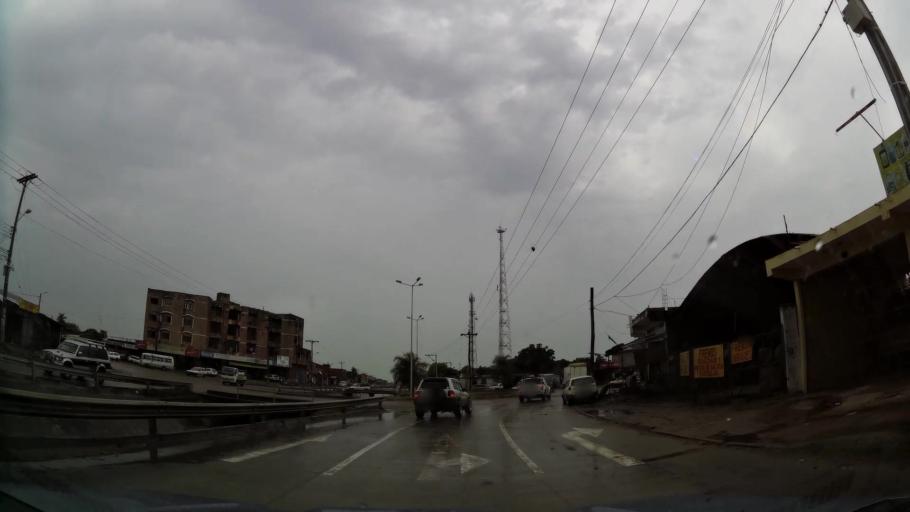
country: BO
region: Santa Cruz
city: Santa Cruz de la Sierra
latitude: -17.8019
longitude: -63.1286
